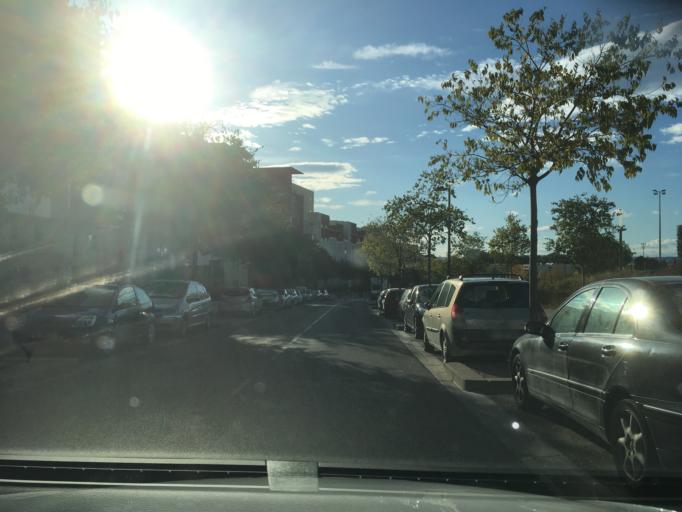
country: FR
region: Languedoc-Roussillon
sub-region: Departement de l'Herault
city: Saint-Jean-de-Vedas
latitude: 43.5919
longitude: 3.8505
